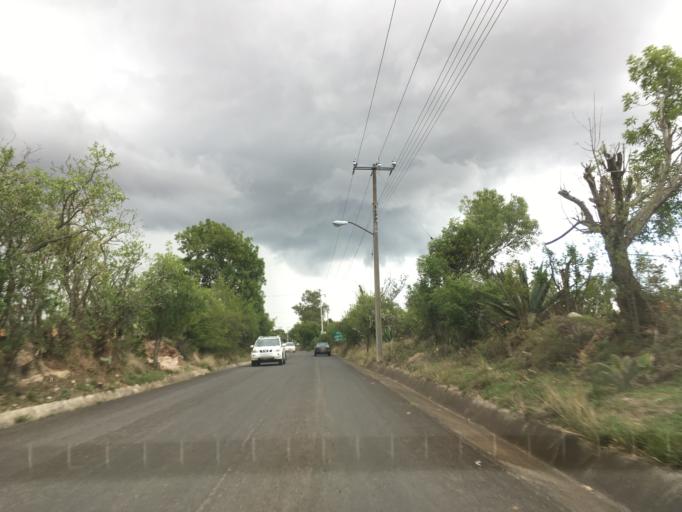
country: MX
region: Michoacan
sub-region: Morelia
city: La Mintzita (Piedra Dura)
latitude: 19.5907
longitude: -101.2737
